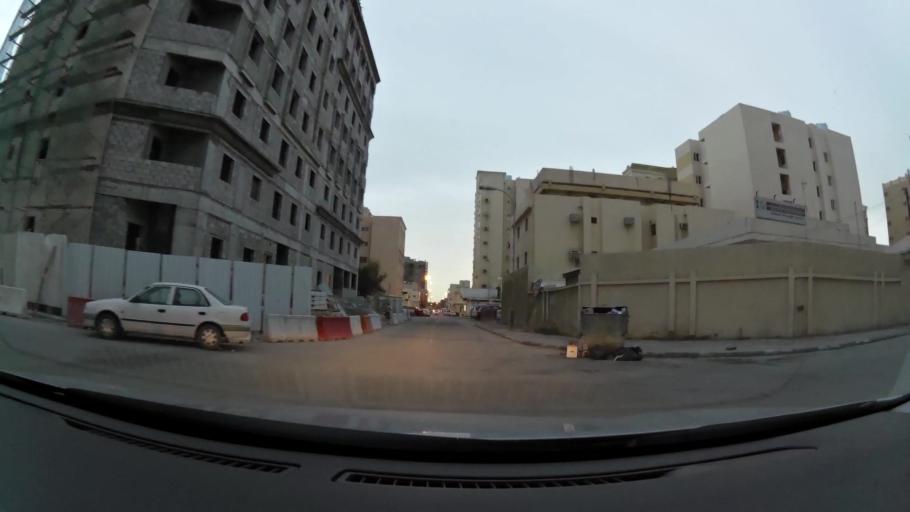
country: QA
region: Baladiyat ad Dawhah
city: Doha
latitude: 25.2720
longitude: 51.5259
